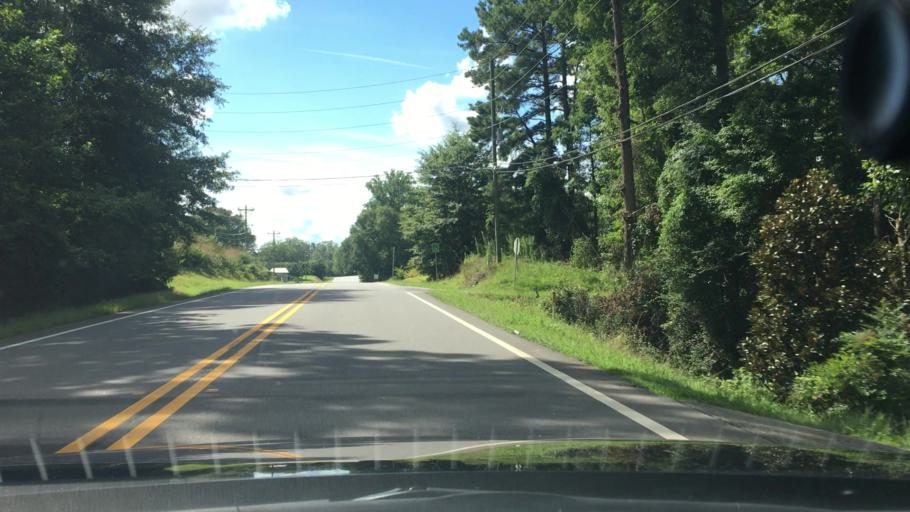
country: US
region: Georgia
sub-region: Butts County
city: Jackson
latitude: 33.2919
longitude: -83.9433
